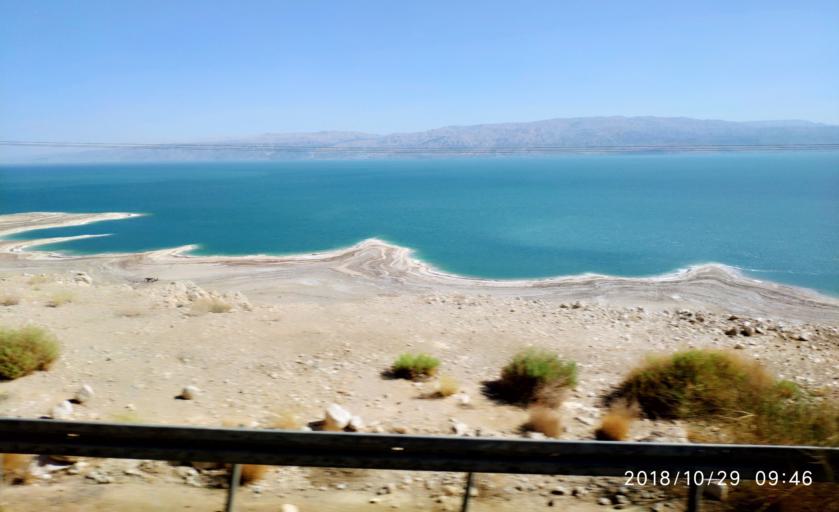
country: PS
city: `Arab ar Rashaydah
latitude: 31.5195
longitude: 35.3926
